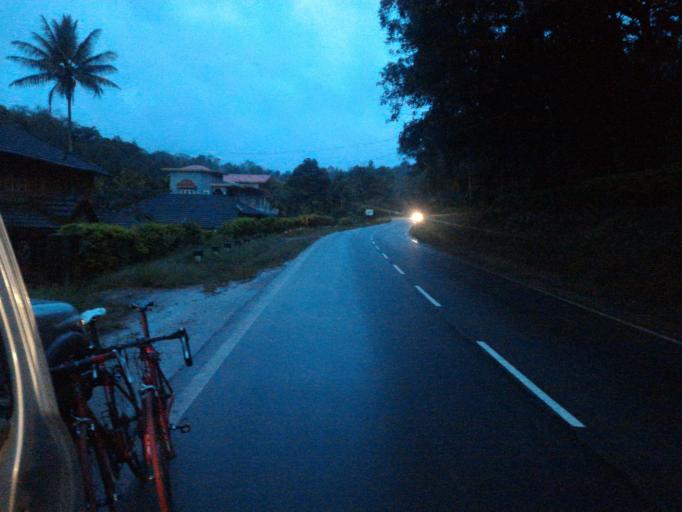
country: IN
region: Karnataka
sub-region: Kodagu
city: Suntikoppa
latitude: 12.4465
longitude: 75.8195
